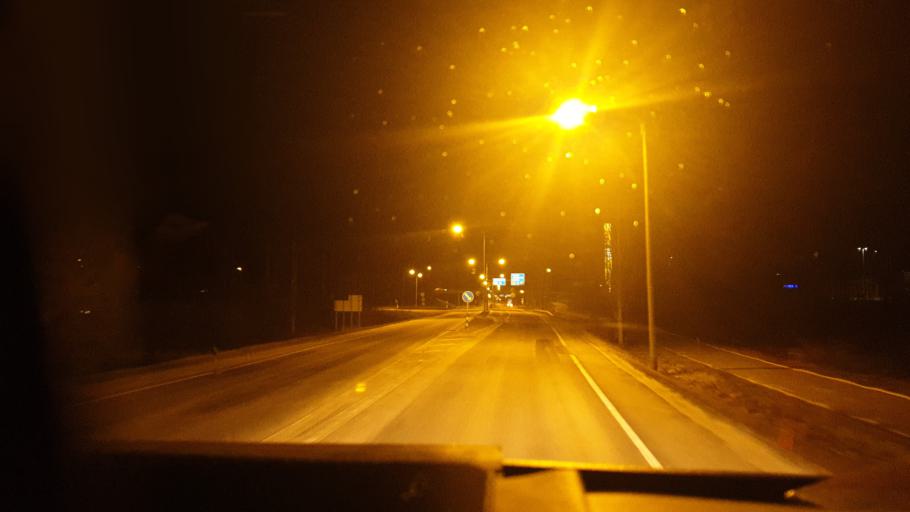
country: FI
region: Southern Ostrobothnia
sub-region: Kuusiokunnat
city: Alavus
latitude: 62.5960
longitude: 23.6132
